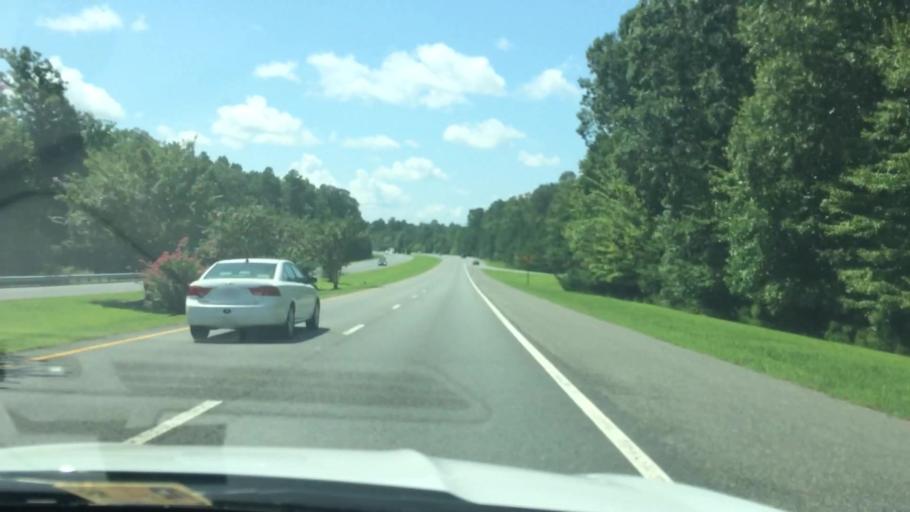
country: US
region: Virginia
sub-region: James City County
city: Williamsburg
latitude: 37.3354
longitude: -76.7517
